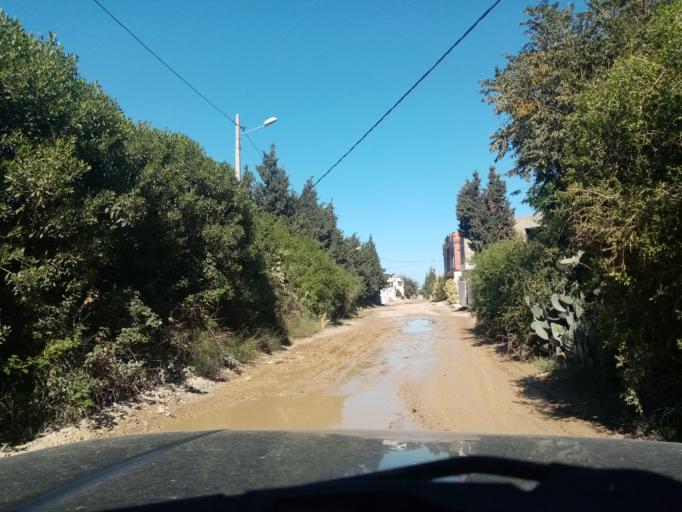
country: TN
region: Nabul
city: Bu `Urqub
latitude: 36.5752
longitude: 10.5727
